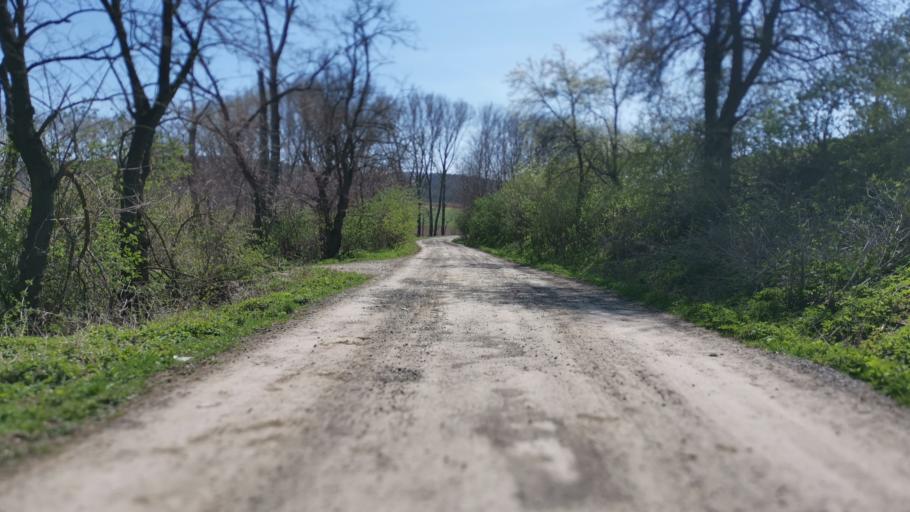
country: SK
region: Trnavsky
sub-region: Okres Senica
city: Senica
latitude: 48.7479
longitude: 17.2823
